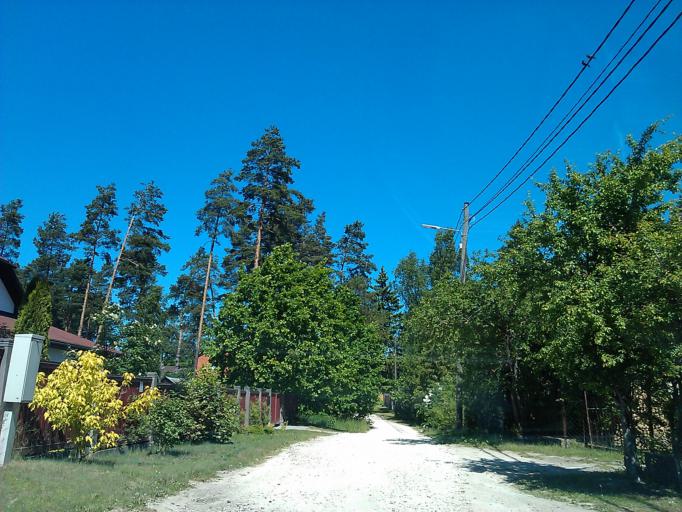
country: LV
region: Riga
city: Bergi
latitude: 57.0057
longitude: 24.3326
